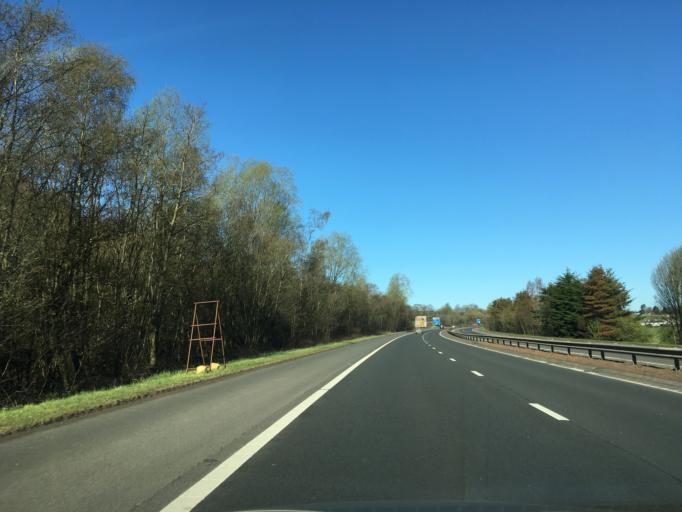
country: GB
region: Scotland
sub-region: Stirling
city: Plean
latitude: 56.0685
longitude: -3.8883
